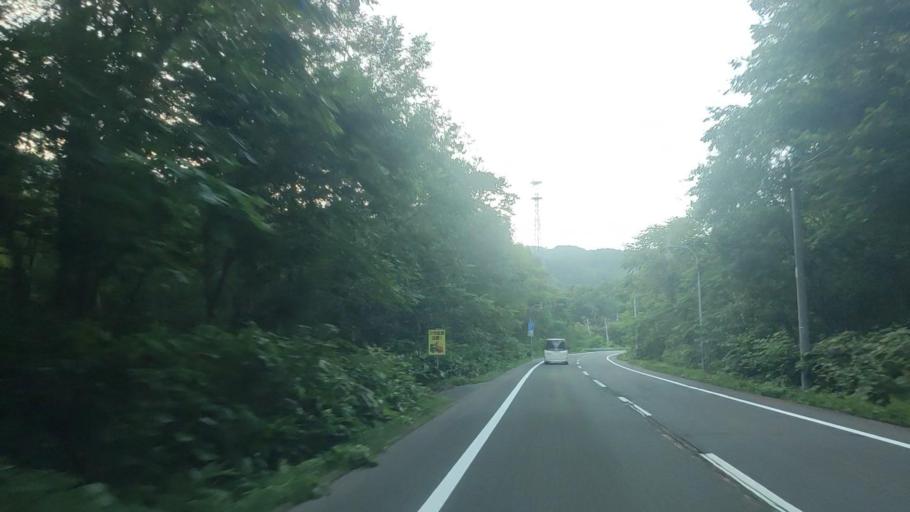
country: JP
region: Hokkaido
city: Ashibetsu
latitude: 43.3454
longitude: 142.1515
